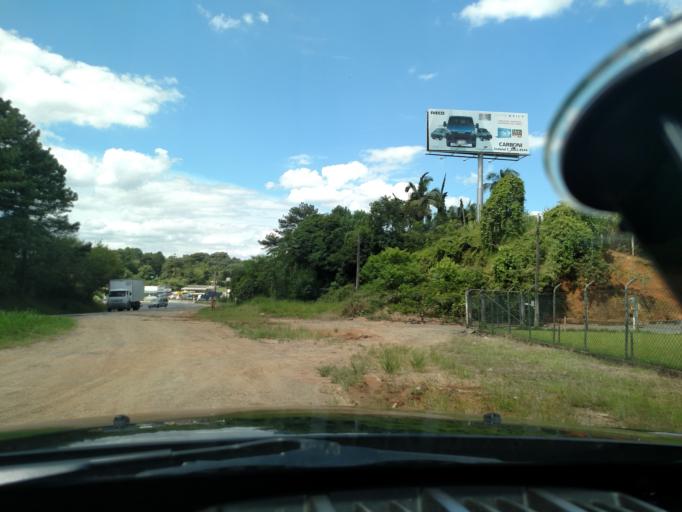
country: BR
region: Santa Catarina
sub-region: Blumenau
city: Blumenau
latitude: -26.8714
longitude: -49.1083
